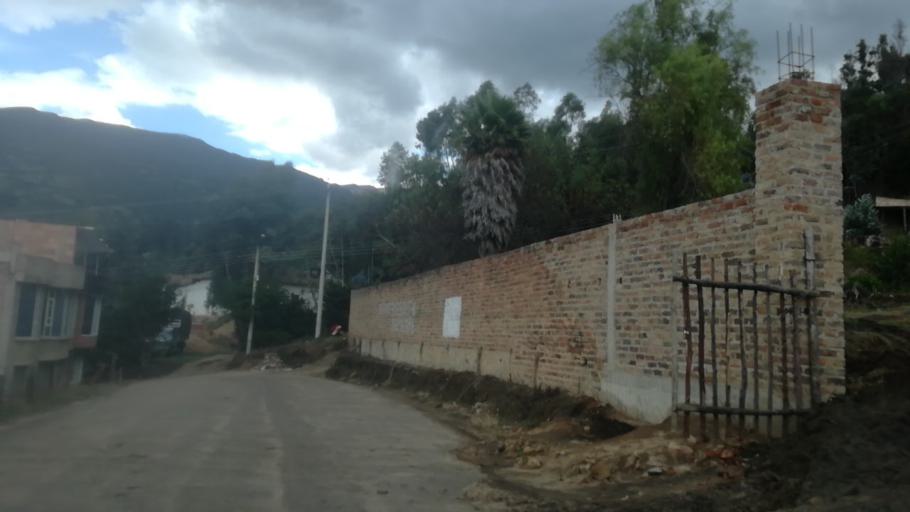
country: CO
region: Boyaca
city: Socha Viejo
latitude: 5.9960
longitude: -72.6944
